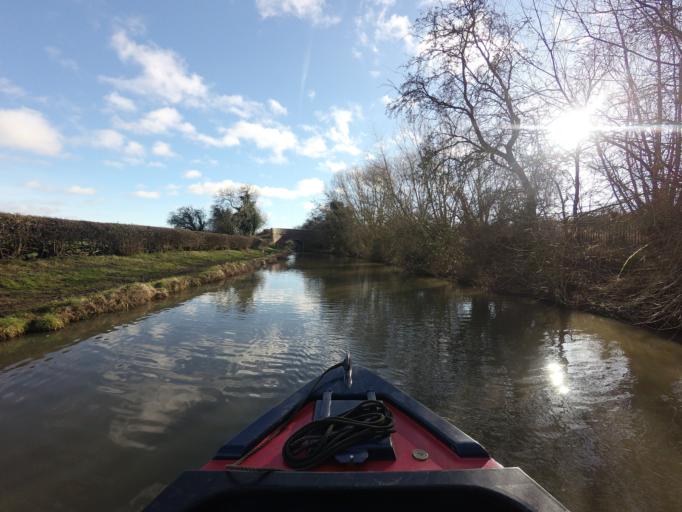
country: GB
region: England
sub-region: Northamptonshire
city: Bugbrooke
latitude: 52.2256
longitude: -1.0716
